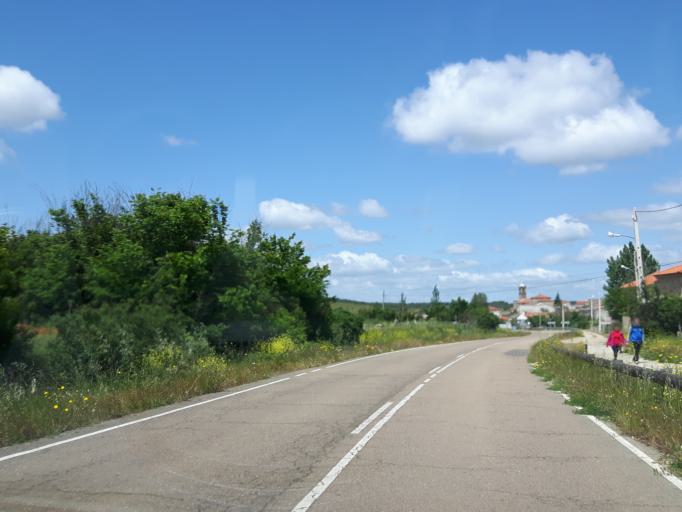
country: ES
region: Castille and Leon
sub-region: Provincia de Salamanca
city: Villar de Ciervo
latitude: 40.7350
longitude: -6.7326
